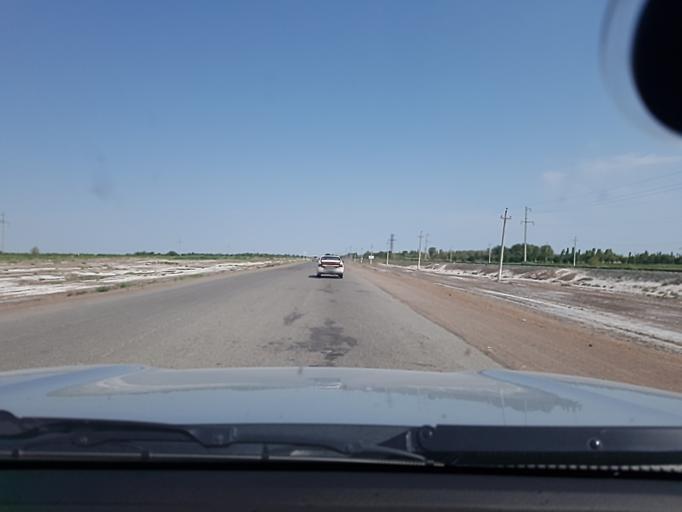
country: UZ
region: Karakalpakstan
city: Xo'jayli Shahri
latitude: 42.2559
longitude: 59.3557
